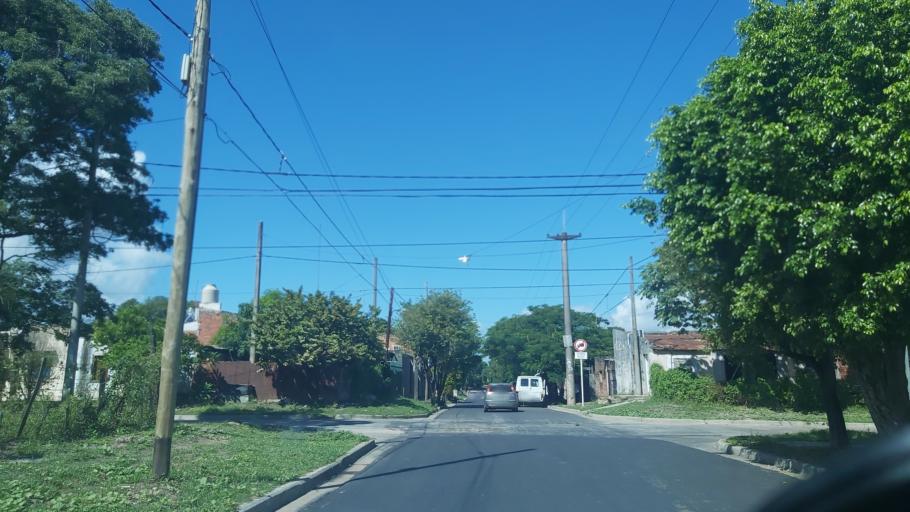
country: AR
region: Corrientes
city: Corrientes
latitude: -27.4814
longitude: -58.8478
